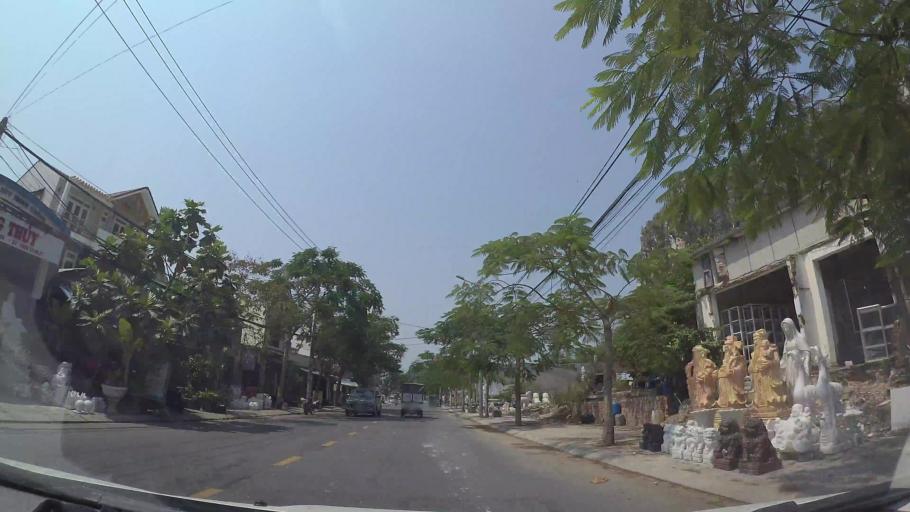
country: VN
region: Da Nang
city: Ngu Hanh Son
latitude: 15.9995
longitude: 108.2607
